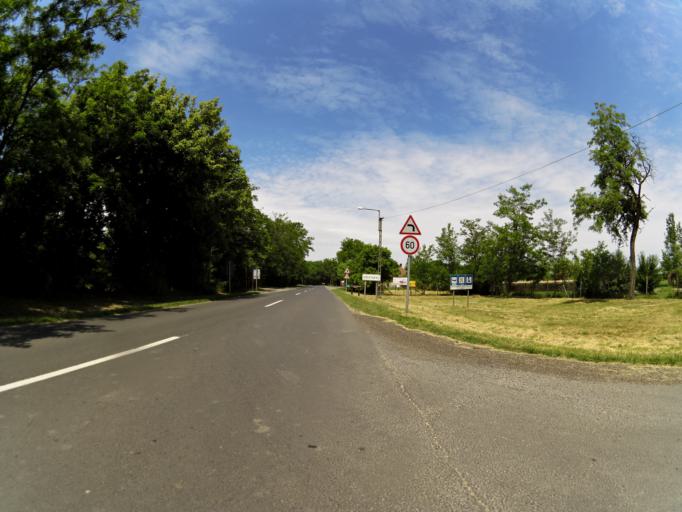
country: HU
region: Csongrad
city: Opusztaszer
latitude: 46.4843
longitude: 20.0844
